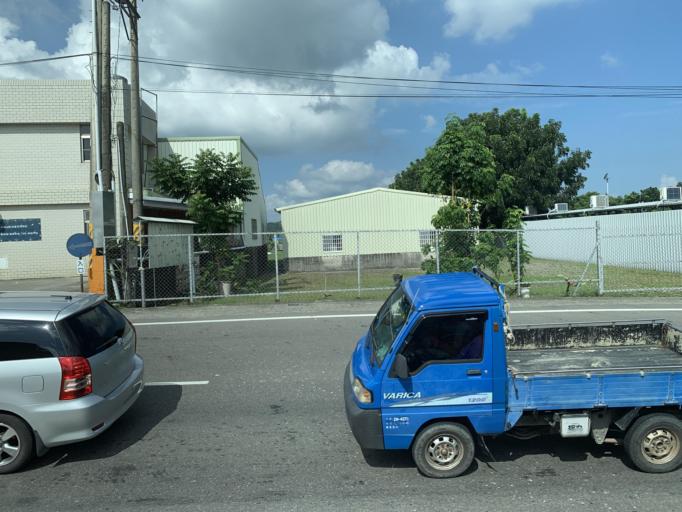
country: TW
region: Taiwan
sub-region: Pingtung
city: Pingtung
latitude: 22.8698
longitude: 120.4951
